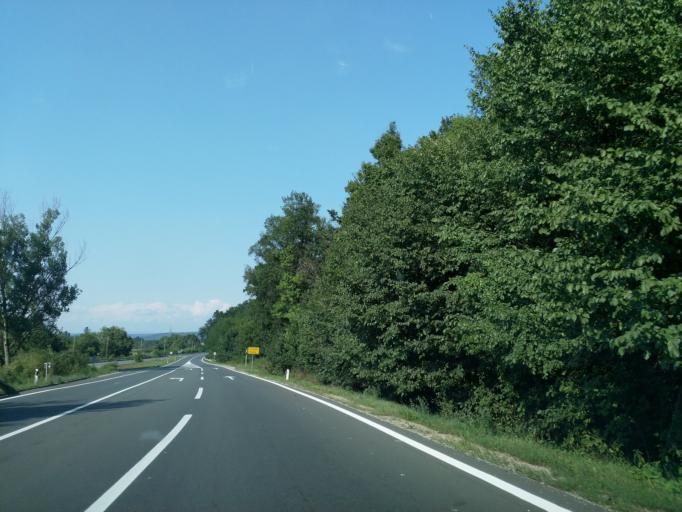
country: RS
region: Central Serbia
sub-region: Rasinski Okrug
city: Cicevac
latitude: 43.6939
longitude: 21.4219
